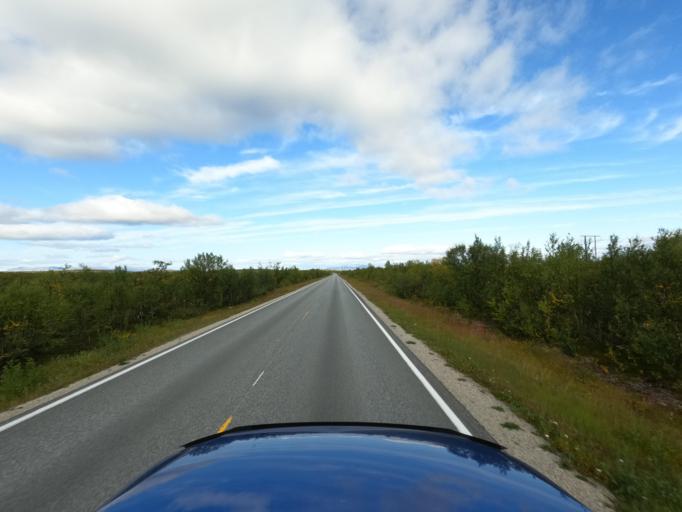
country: NO
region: Finnmark Fylke
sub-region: Karasjok
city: Karasjohka
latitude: 69.6584
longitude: 25.2773
